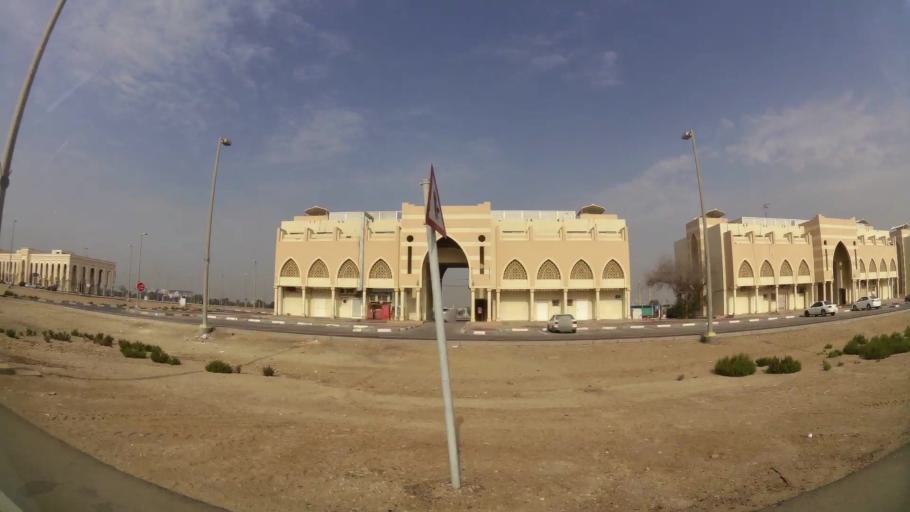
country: AE
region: Abu Dhabi
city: Abu Dhabi
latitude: 24.6681
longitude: 54.7635
